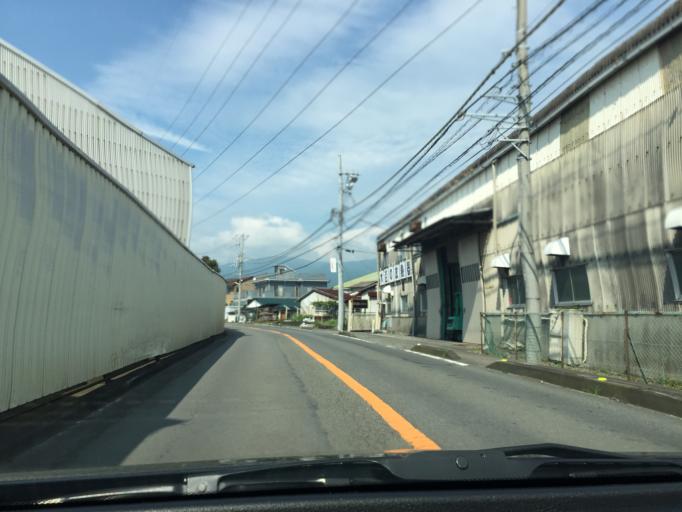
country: JP
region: Shizuoka
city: Mishima
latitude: 35.1585
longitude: 138.9097
